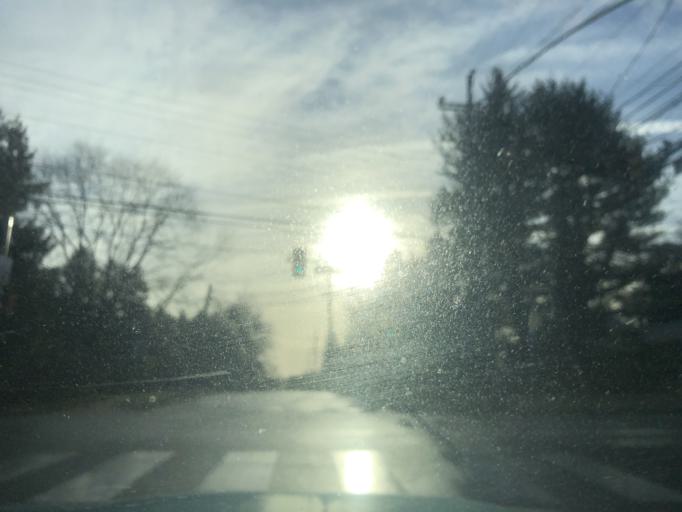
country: US
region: Pennsylvania
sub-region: Montgomery County
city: Fort Washington
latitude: 40.1471
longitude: -75.2020
